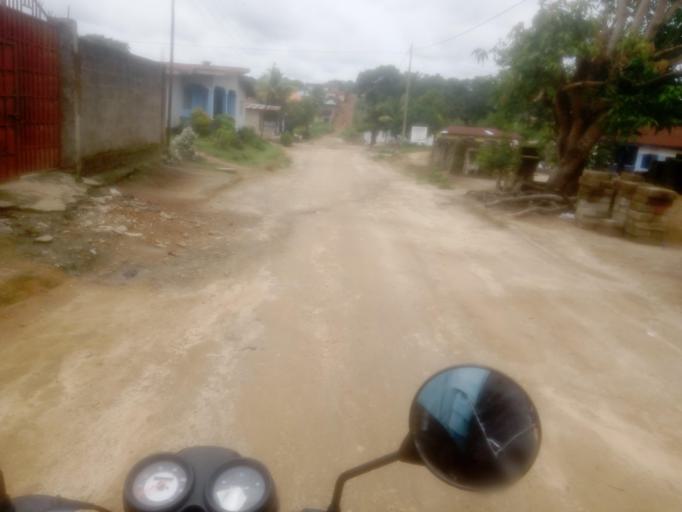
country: SL
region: Southern Province
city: Bo
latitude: 7.9481
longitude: -11.7519
